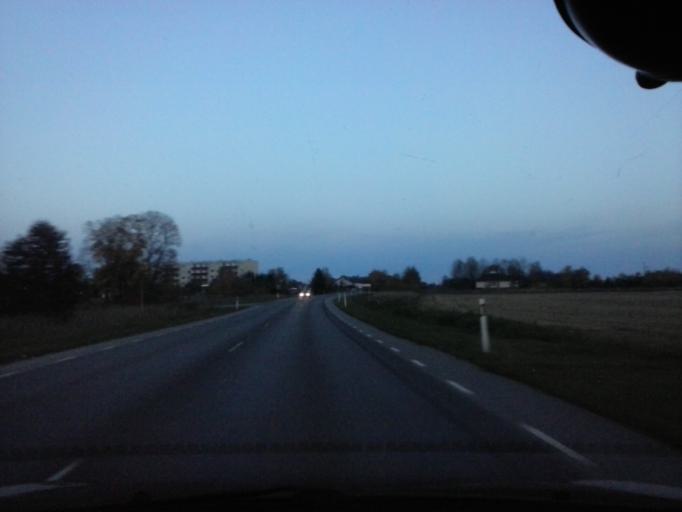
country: EE
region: Raplamaa
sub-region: Rapla vald
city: Rapla
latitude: 58.9959
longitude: 24.7776
